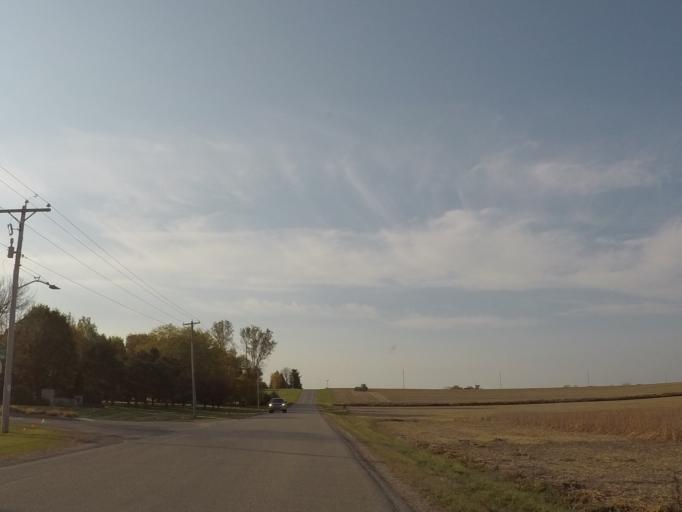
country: US
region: Wisconsin
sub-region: Dane County
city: Cross Plains
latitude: 43.0547
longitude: -89.6010
